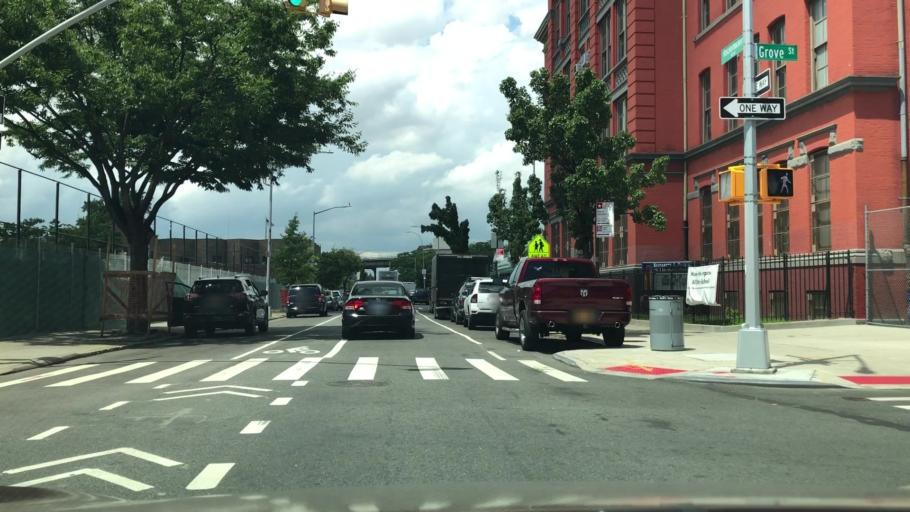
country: US
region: New York
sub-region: Kings County
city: East New York
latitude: 40.6977
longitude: -73.9163
